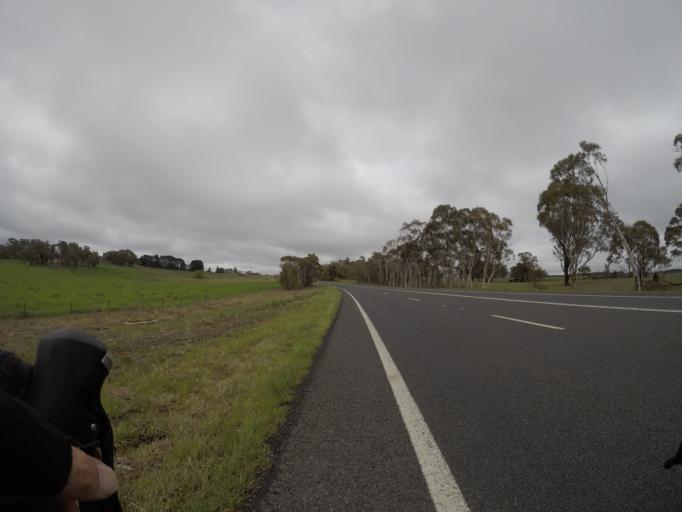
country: AU
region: New South Wales
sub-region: Lithgow
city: Portland
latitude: -33.4461
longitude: 149.9936
